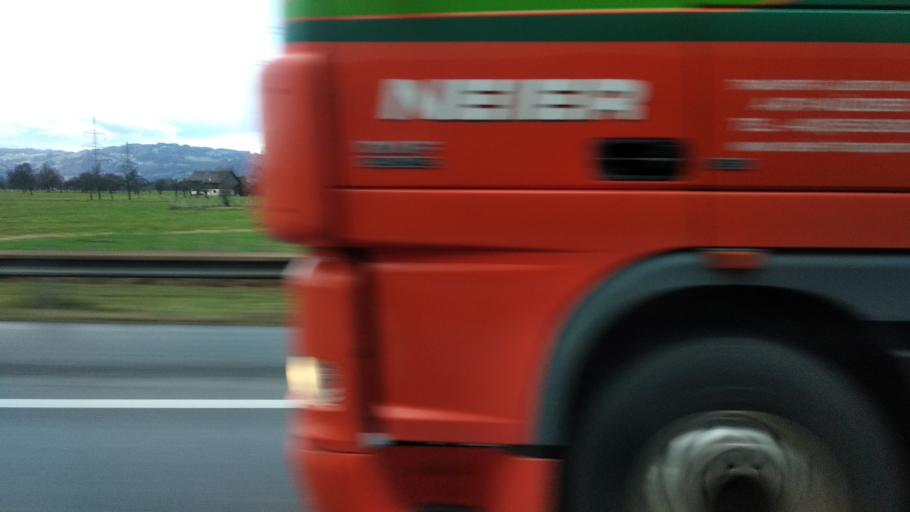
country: AT
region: Vorarlberg
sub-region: Politischer Bezirk Dornbirn
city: Dornbirn
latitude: 47.4272
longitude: 9.7175
